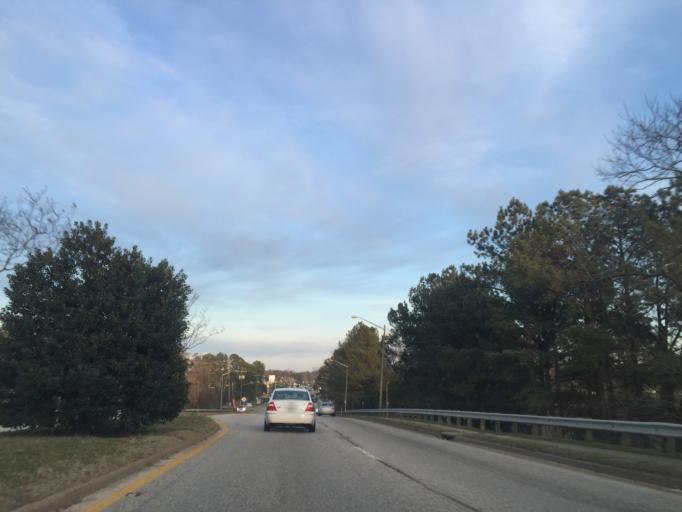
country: US
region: Virginia
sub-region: York County
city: Yorktown
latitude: 37.1058
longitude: -76.5028
